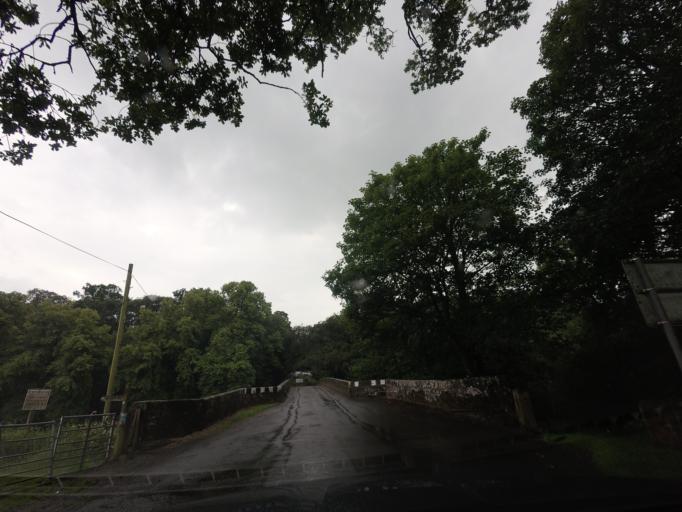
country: GB
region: Scotland
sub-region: Dumfries and Galloway
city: Annan
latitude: 55.0421
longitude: -3.3102
